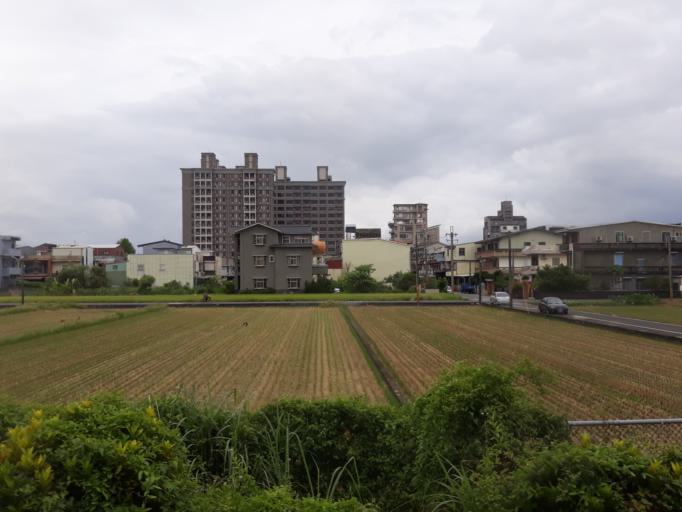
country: TW
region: Taiwan
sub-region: Yilan
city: Yilan
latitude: 24.6907
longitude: 121.7750
